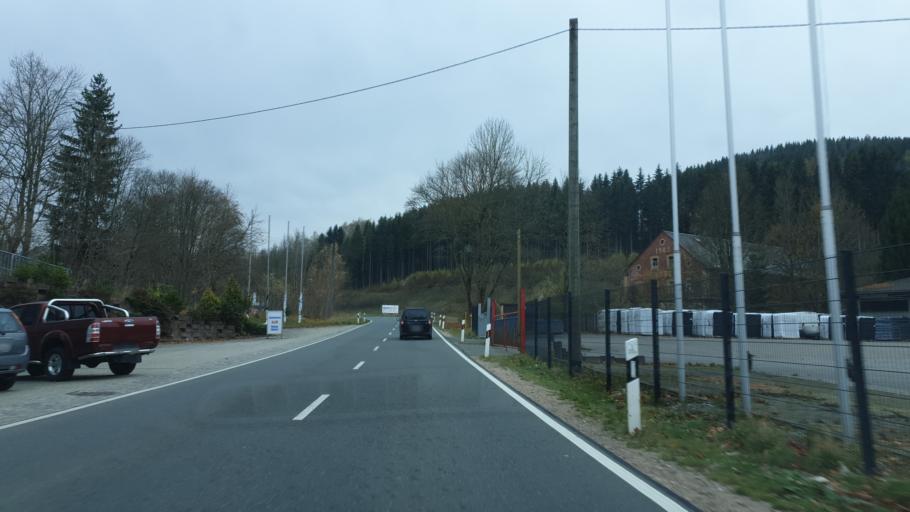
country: DE
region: Saxony
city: Johanngeorgenstadt
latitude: 50.4406
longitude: 12.7272
